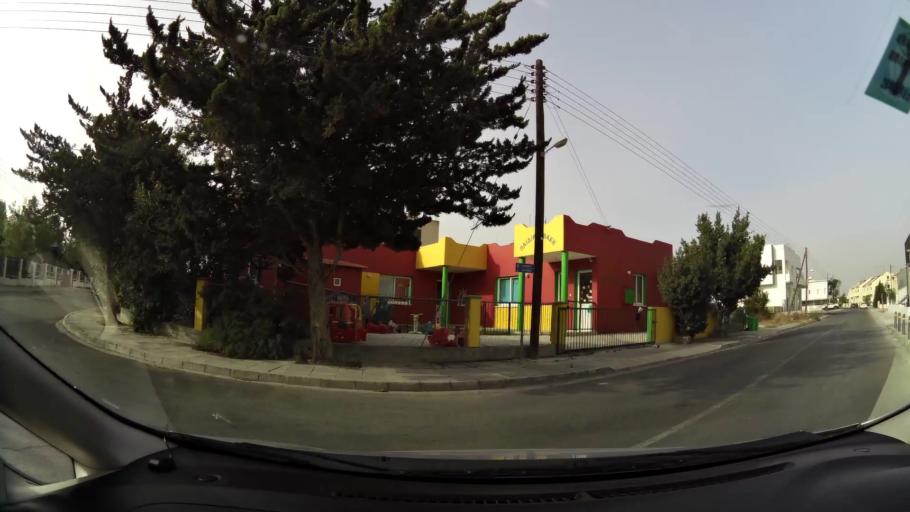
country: CY
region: Lefkosia
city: Geri
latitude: 35.0659
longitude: 33.3875
